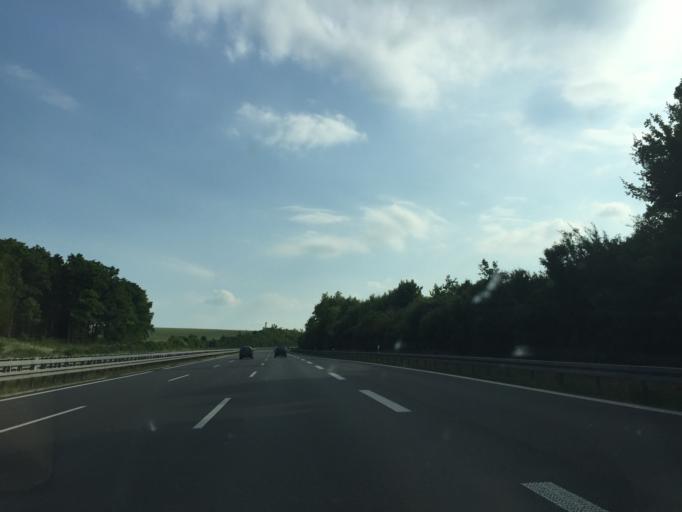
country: DE
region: Baden-Wuerttemberg
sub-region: Regierungsbezirk Stuttgart
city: Tauberbischofsheim
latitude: 49.5908
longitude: 9.6684
